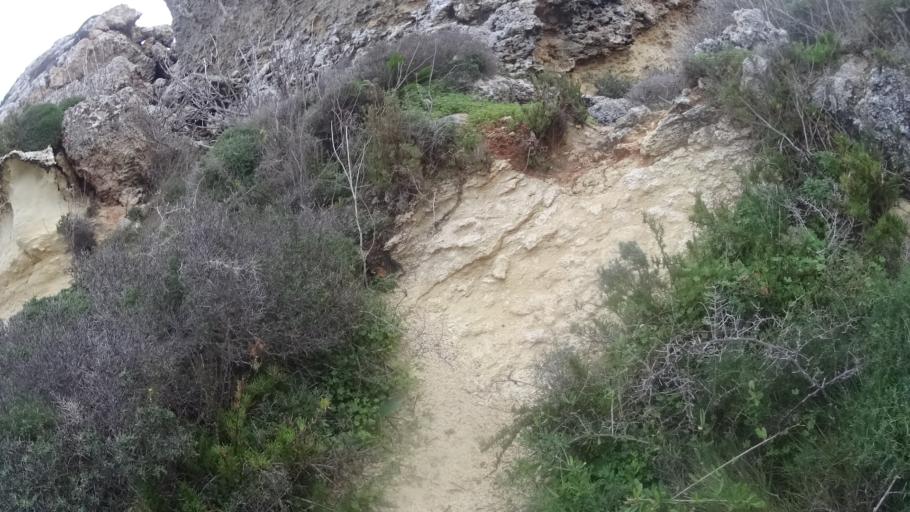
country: MT
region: Il-Mellieha
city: Mellieha
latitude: 35.9778
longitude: 14.3273
